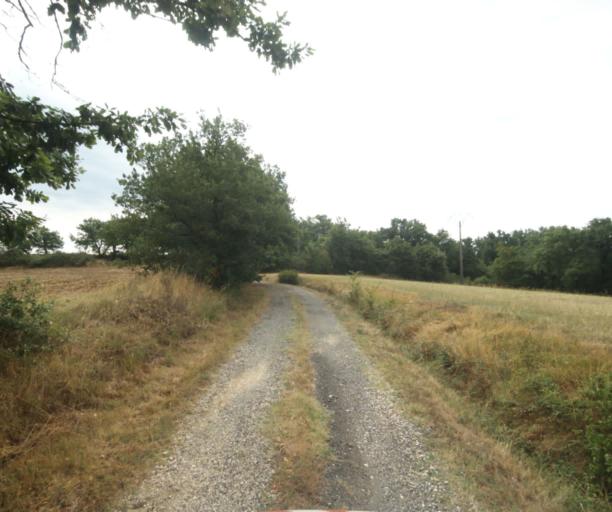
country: FR
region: Midi-Pyrenees
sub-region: Departement de la Haute-Garonne
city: Revel
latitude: 43.4397
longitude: 1.9740
